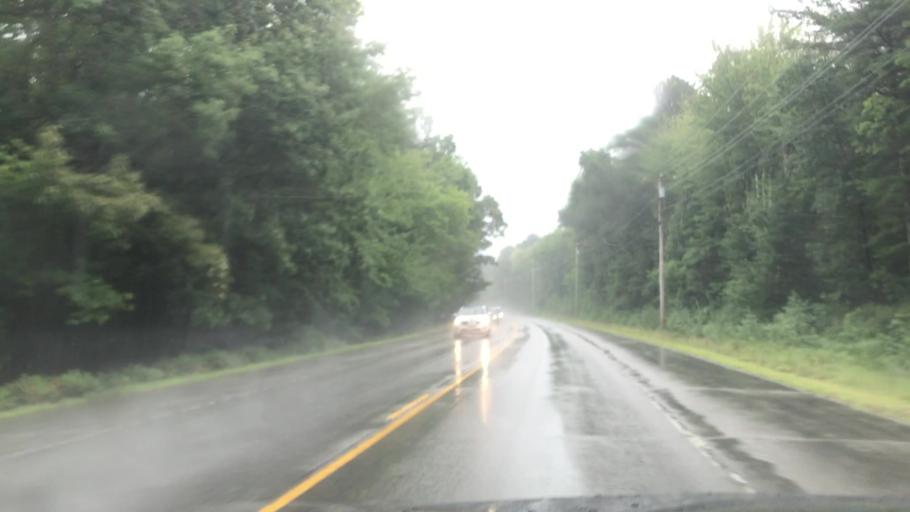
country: US
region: Maine
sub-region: York County
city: Wells Beach Station
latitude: 43.3081
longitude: -70.6599
